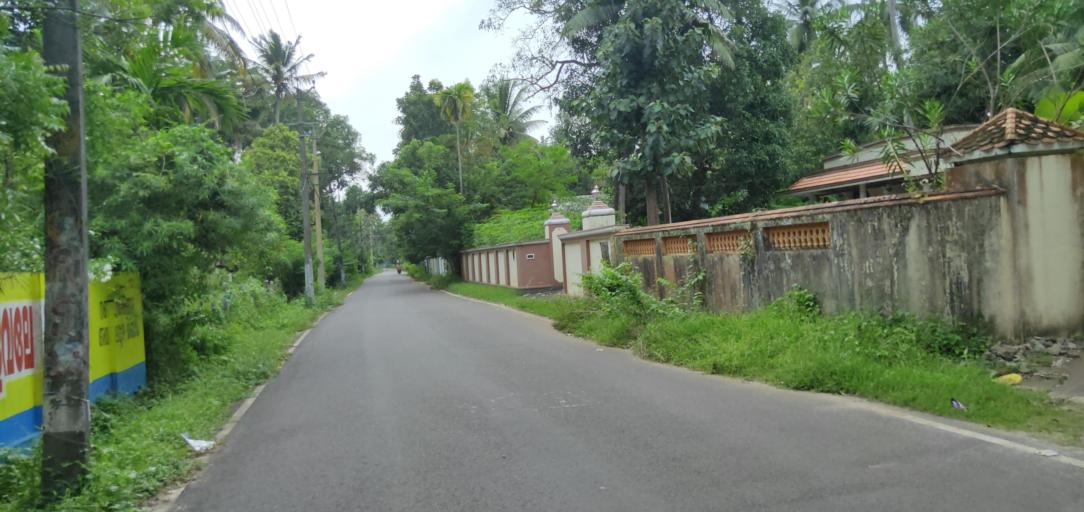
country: IN
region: Kerala
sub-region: Alappuzha
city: Kayankulam
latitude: 9.2152
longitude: 76.4550
